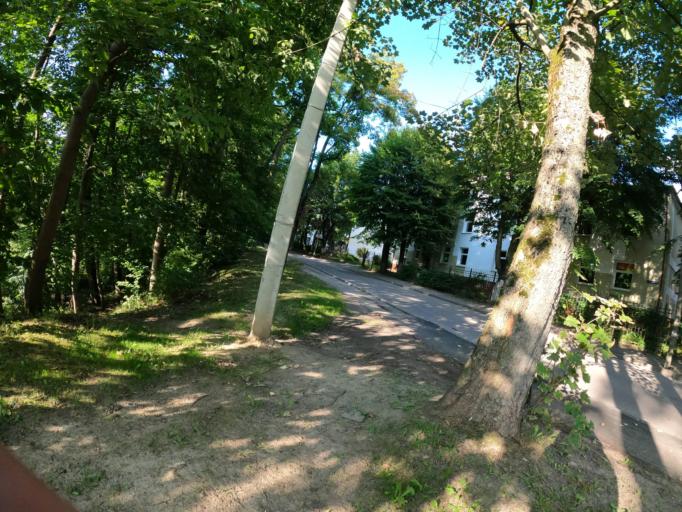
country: RU
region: Kaliningrad
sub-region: Gorod Kaliningrad
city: Kaliningrad
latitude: 54.7235
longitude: 20.4573
